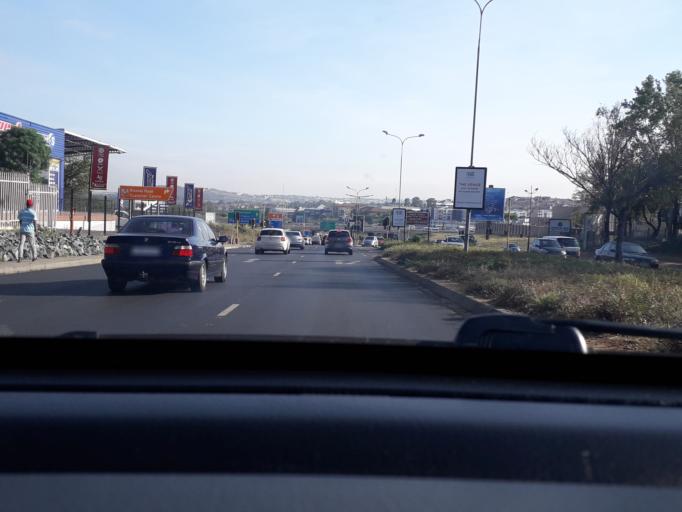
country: ZA
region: Gauteng
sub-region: City of Johannesburg Metropolitan Municipality
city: Midrand
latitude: -26.0417
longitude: 28.0602
